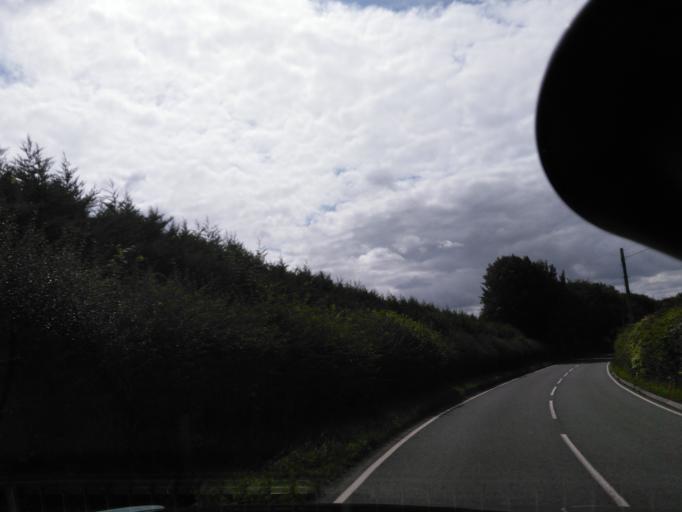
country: GB
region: England
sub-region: Dorset
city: Shaftesbury
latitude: 50.9393
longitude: -2.1593
